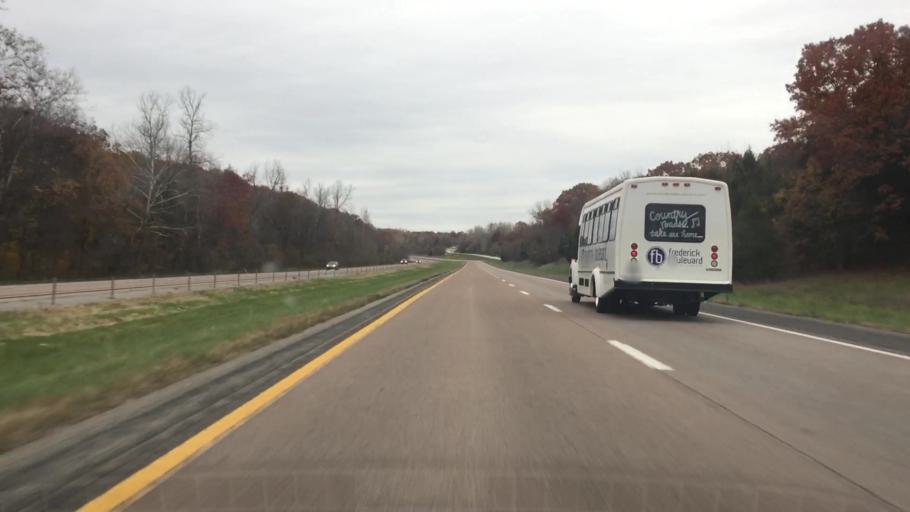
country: US
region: Missouri
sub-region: Cole County
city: Jefferson City
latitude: 38.6624
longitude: -92.2251
